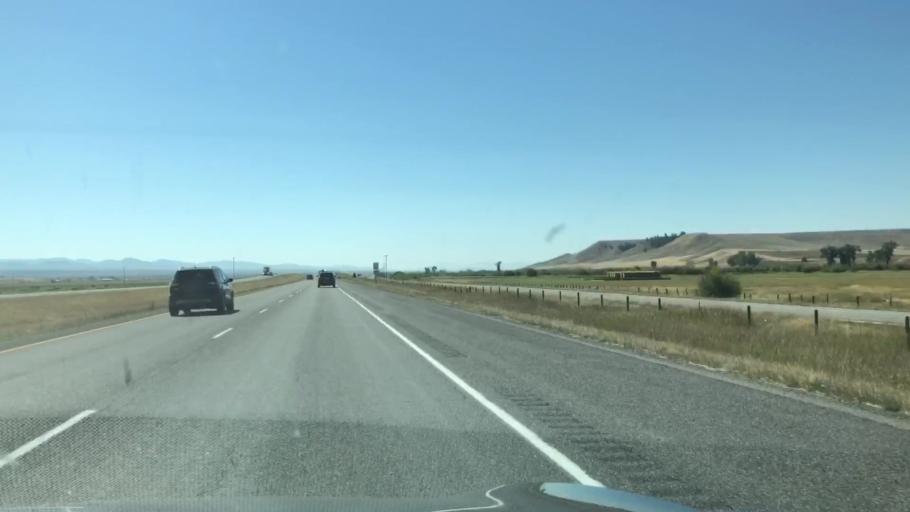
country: US
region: Montana
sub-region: Powell County
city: Deer Lodge
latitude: 46.4811
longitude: -112.7229
